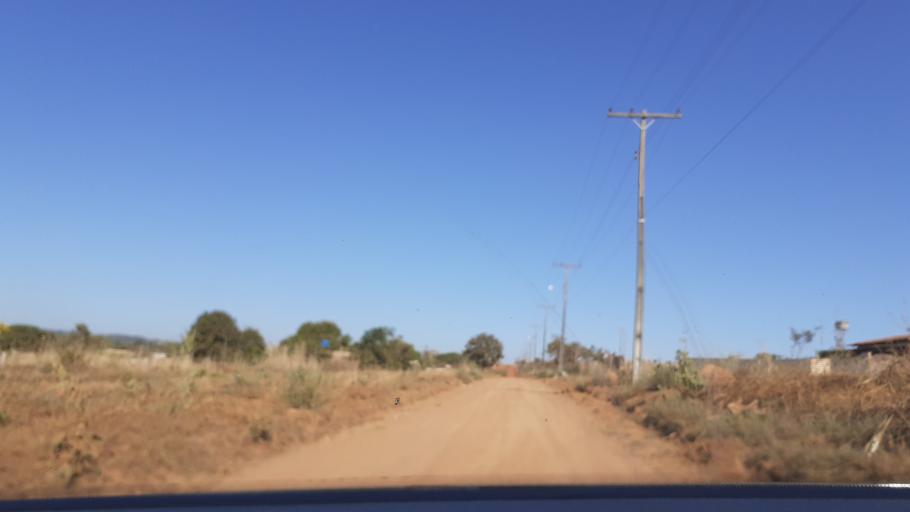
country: BR
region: Goias
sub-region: Aparecida De Goiania
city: Aparecida de Goiania
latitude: -16.8705
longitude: -49.2644
